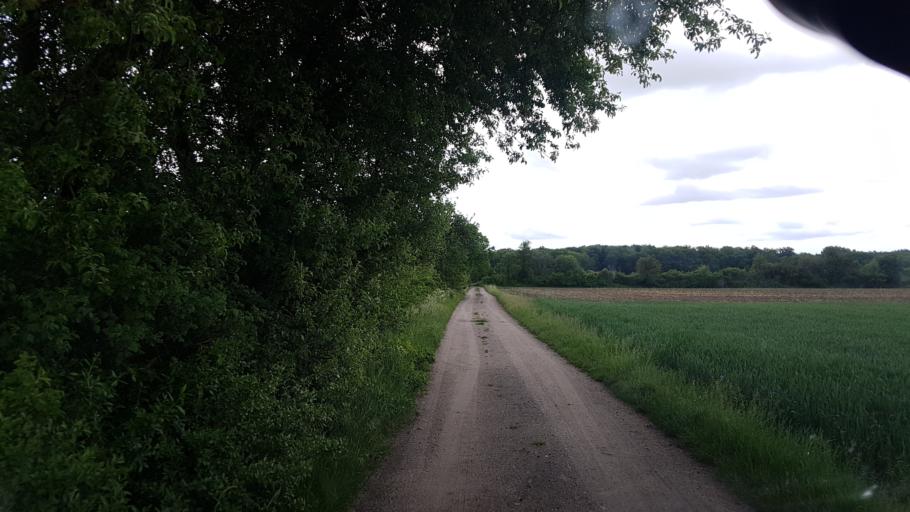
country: DE
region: Brandenburg
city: Doberlug-Kirchhain
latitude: 51.6284
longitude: 13.5402
